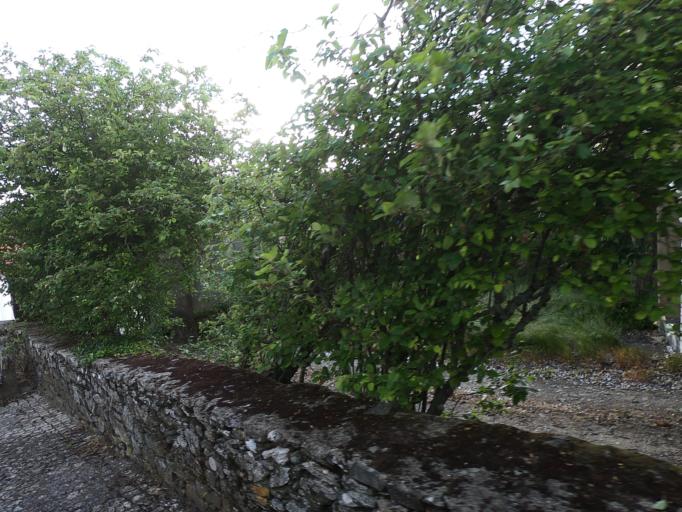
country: PT
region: Vila Real
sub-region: Sabrosa
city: Vilela
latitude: 41.2079
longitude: -7.6571
